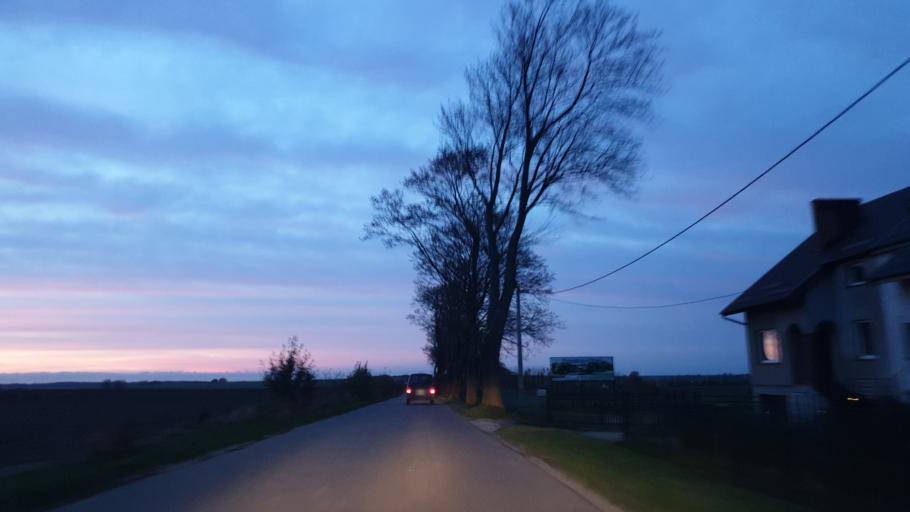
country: PL
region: Pomeranian Voivodeship
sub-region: Powiat pucki
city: Krokowa
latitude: 54.7776
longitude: 18.2065
